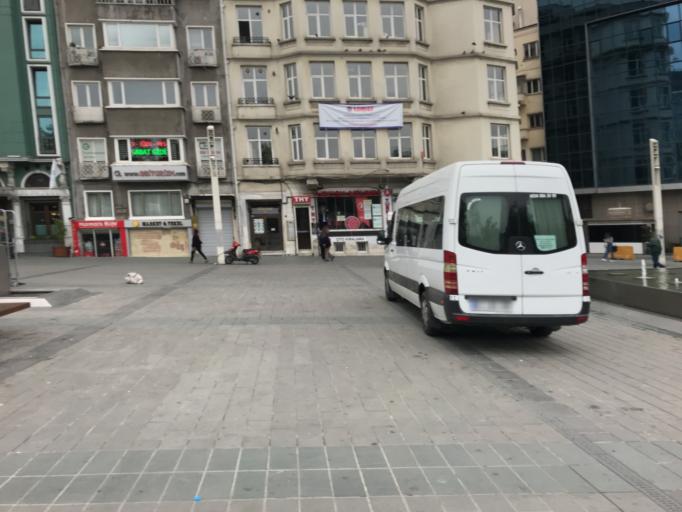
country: TR
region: Istanbul
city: Sisli
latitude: 41.0390
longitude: 28.9861
